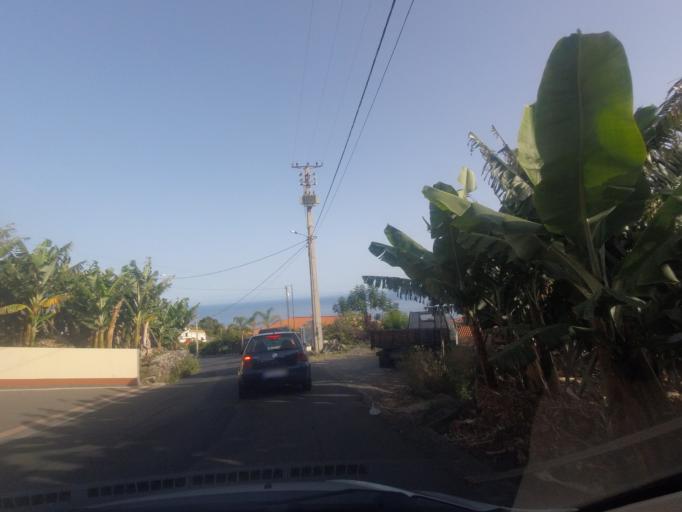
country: PT
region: Madeira
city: Ponta do Sol
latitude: 32.6805
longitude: -17.0823
